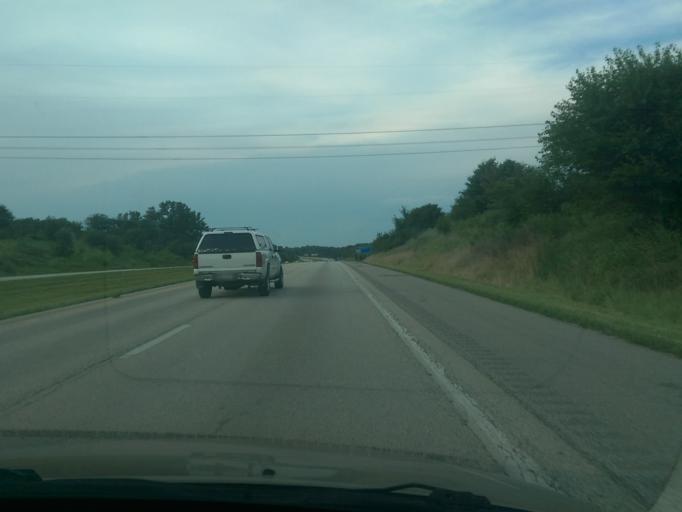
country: US
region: Missouri
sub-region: Andrew County
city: Country Club Village
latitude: 39.8436
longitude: -94.8052
